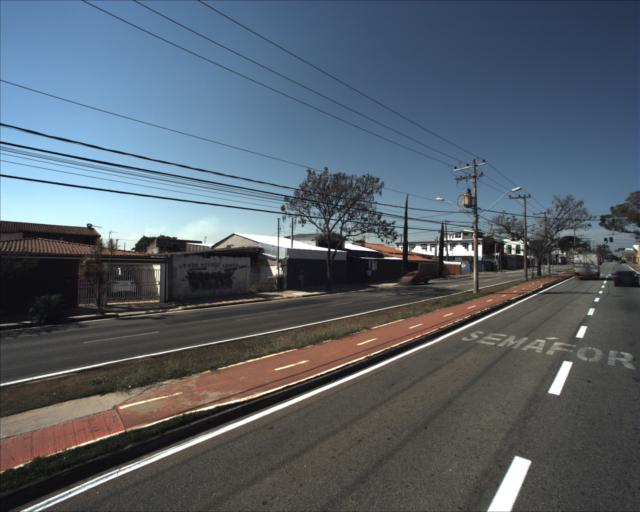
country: BR
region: Sao Paulo
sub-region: Sorocaba
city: Sorocaba
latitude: -23.4836
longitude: -47.4830
